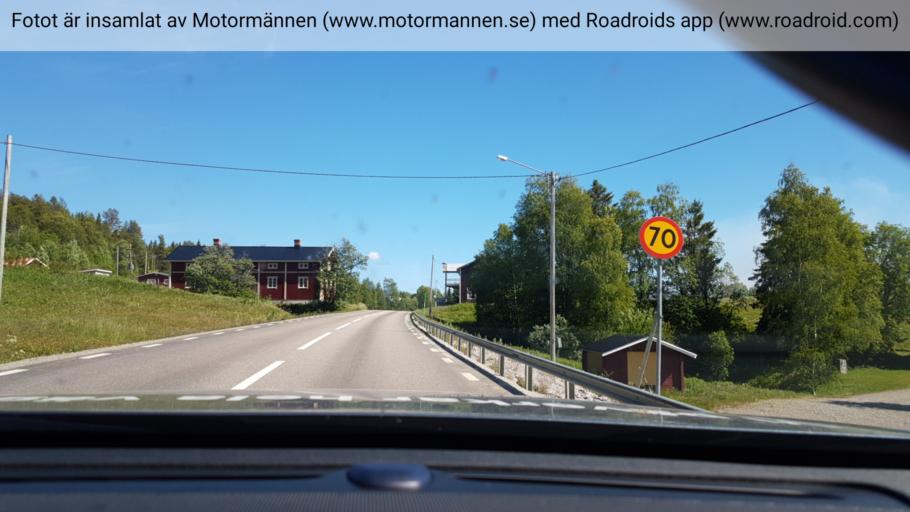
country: SE
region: Vaesterbotten
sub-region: Asele Kommun
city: Insjon
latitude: 64.7167
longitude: 17.6776
